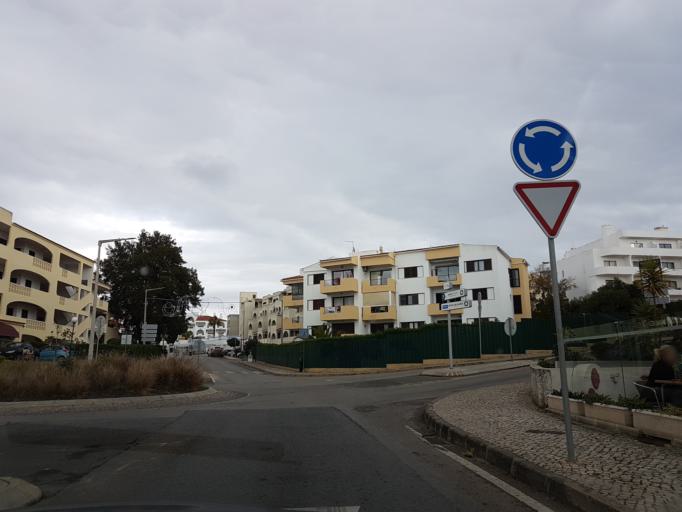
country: PT
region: Faro
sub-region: Albufeira
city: Albufeira
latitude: 37.0912
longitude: -8.2342
